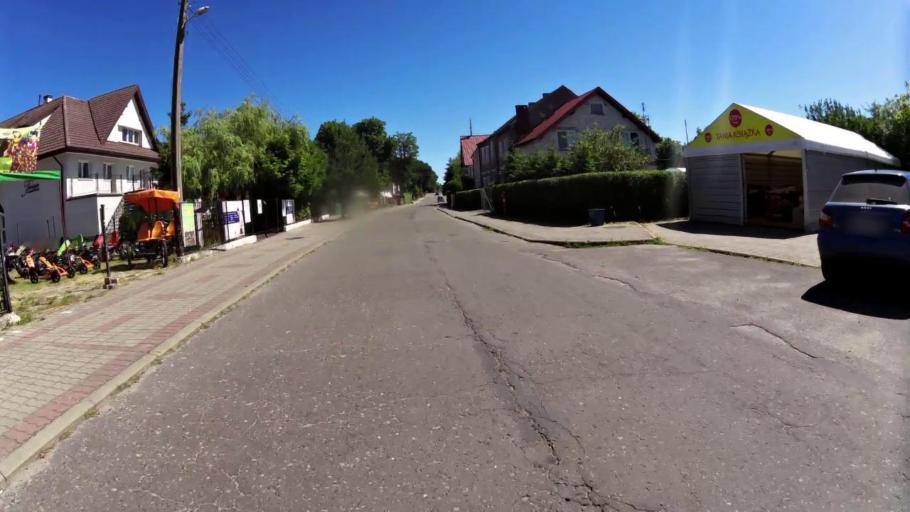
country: PL
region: West Pomeranian Voivodeship
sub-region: Powiat gryficki
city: Pobierowo
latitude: 54.0693
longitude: 14.9718
